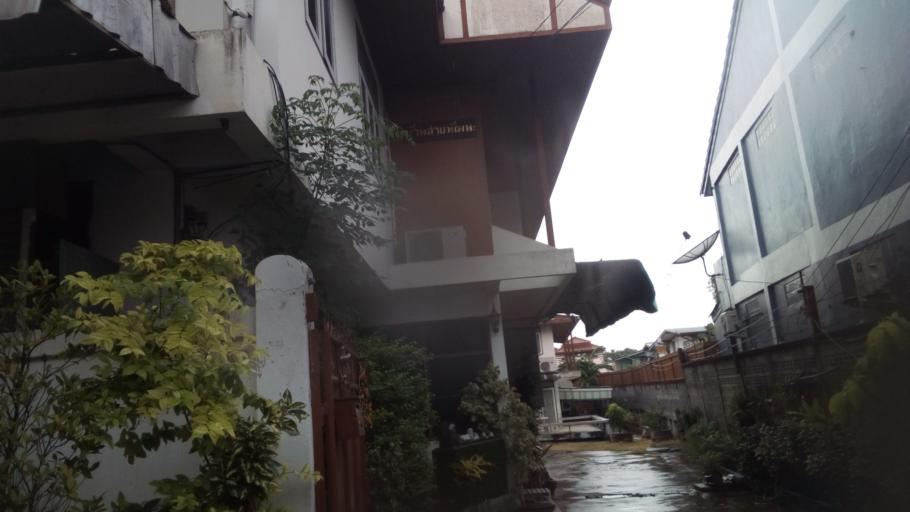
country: TH
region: Phra Nakhon Si Ayutthaya
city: Phra Nakhon Si Ayutthaya
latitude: 14.3586
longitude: 100.5506
